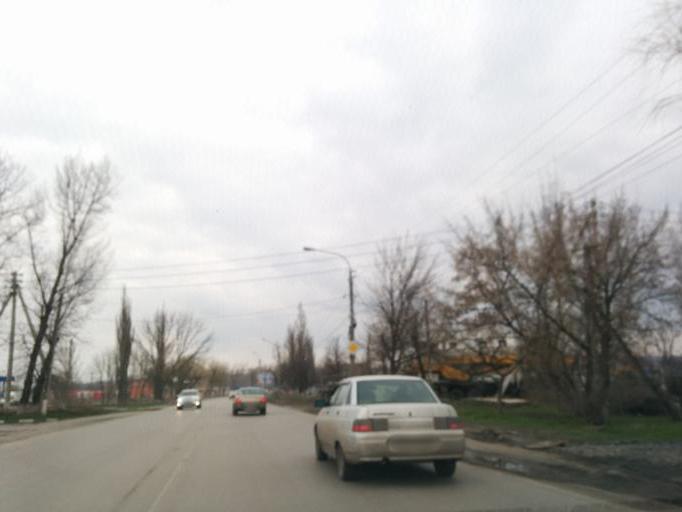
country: RU
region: Rostov
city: Novocherkassk
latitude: 47.4524
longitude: 40.1026
